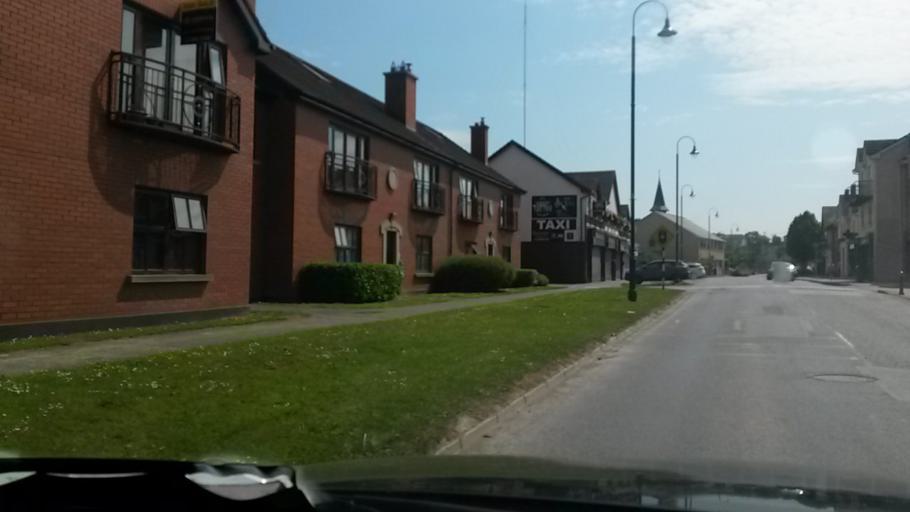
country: IE
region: Leinster
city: Donabate
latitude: 53.4878
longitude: -6.1483
